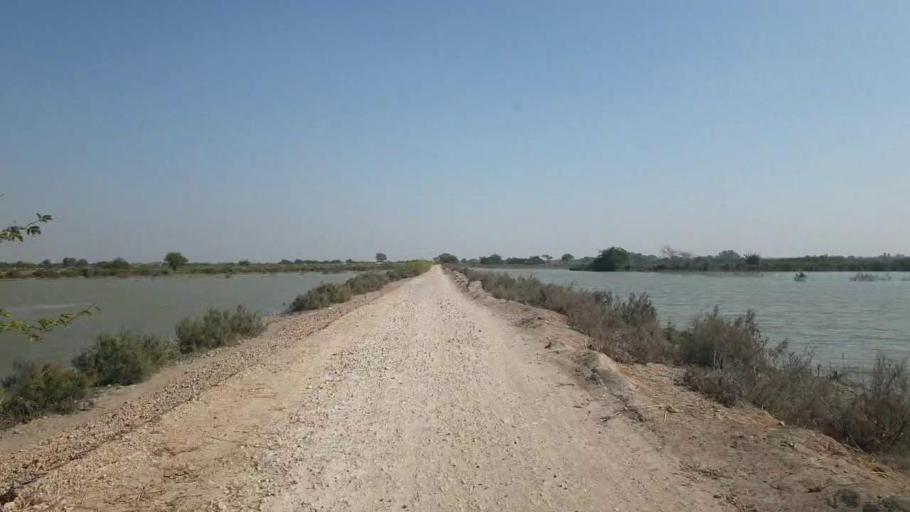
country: PK
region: Sindh
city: Talhar
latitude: 24.7755
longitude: 68.7805
